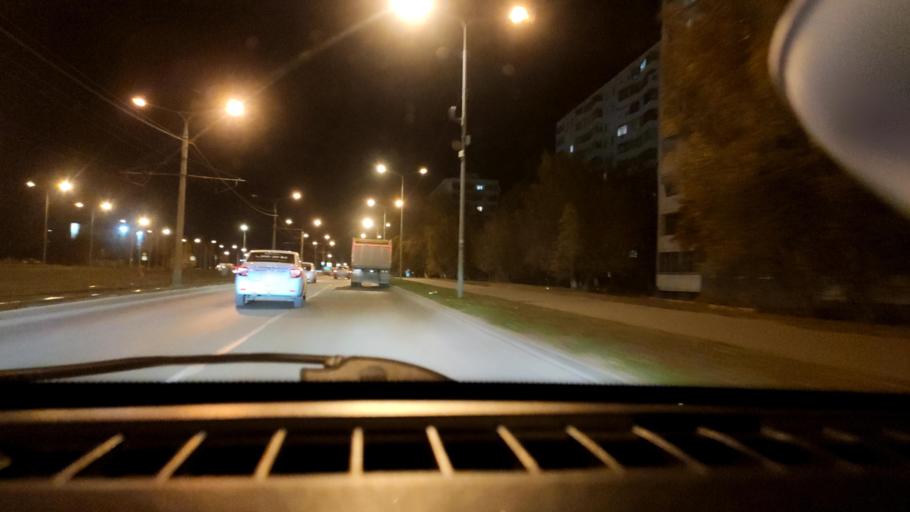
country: RU
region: Samara
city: Samara
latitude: 53.2634
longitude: 50.2345
